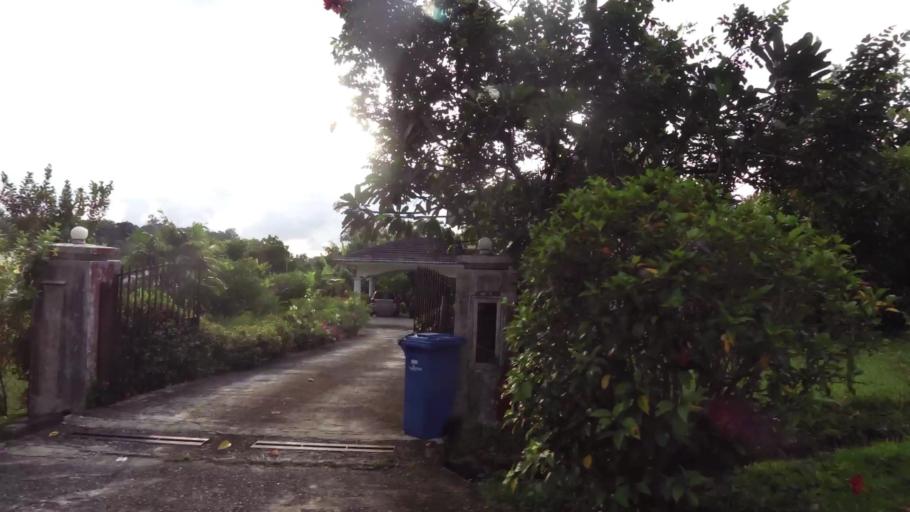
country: BN
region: Brunei and Muara
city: Bandar Seri Begawan
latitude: 4.9498
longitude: 114.9787
